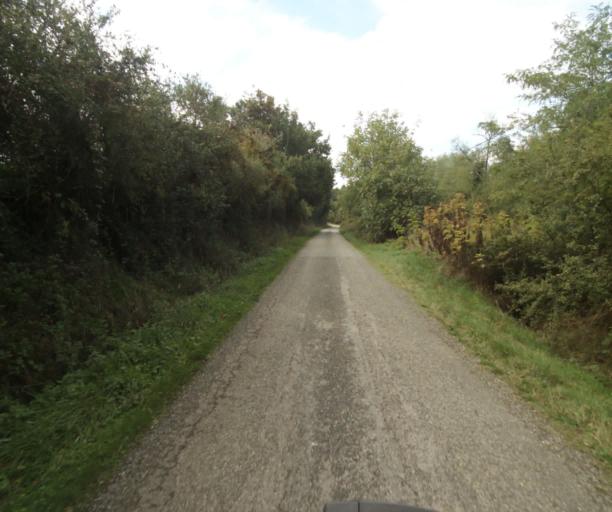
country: FR
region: Midi-Pyrenees
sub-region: Departement du Tarn-et-Garonne
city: Saint-Porquier
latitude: 43.9547
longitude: 1.1505
